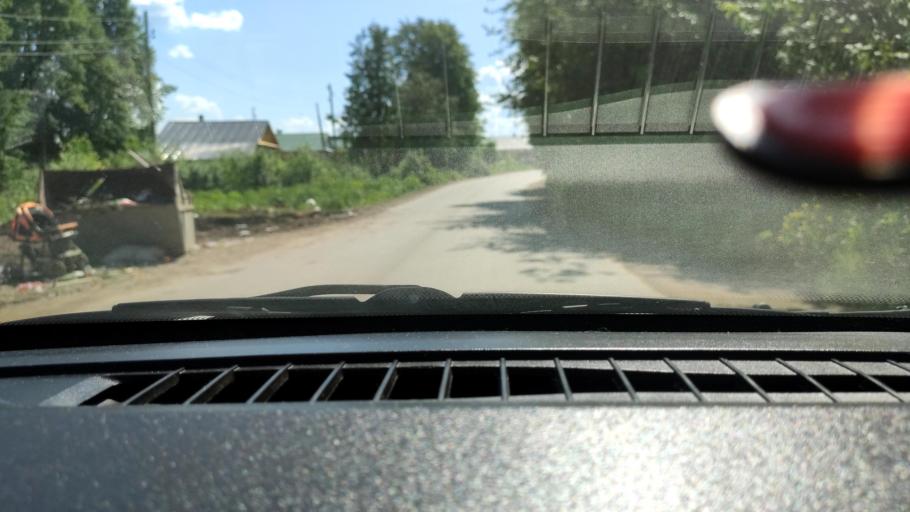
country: RU
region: Perm
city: Sylva
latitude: 58.0337
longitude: 56.7747
